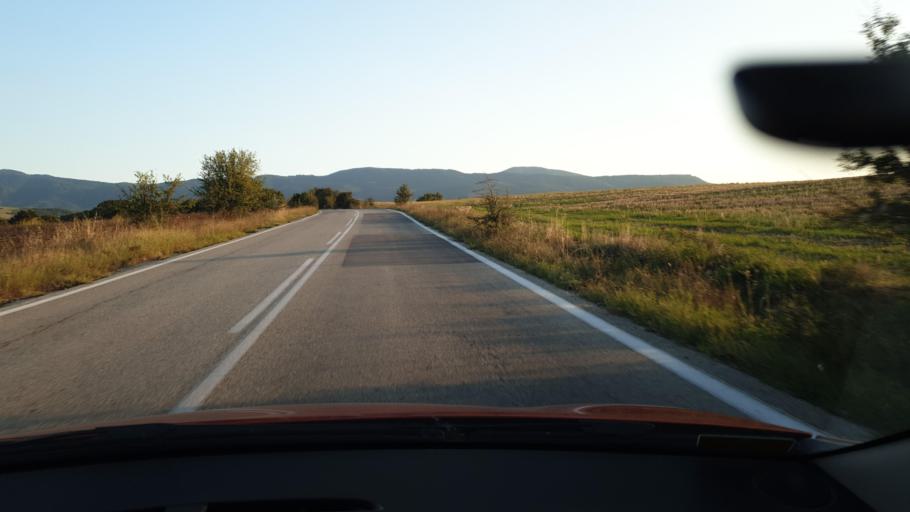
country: GR
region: Central Macedonia
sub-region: Nomos Thessalonikis
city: Nea Apollonia
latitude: 40.5400
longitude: 23.4691
